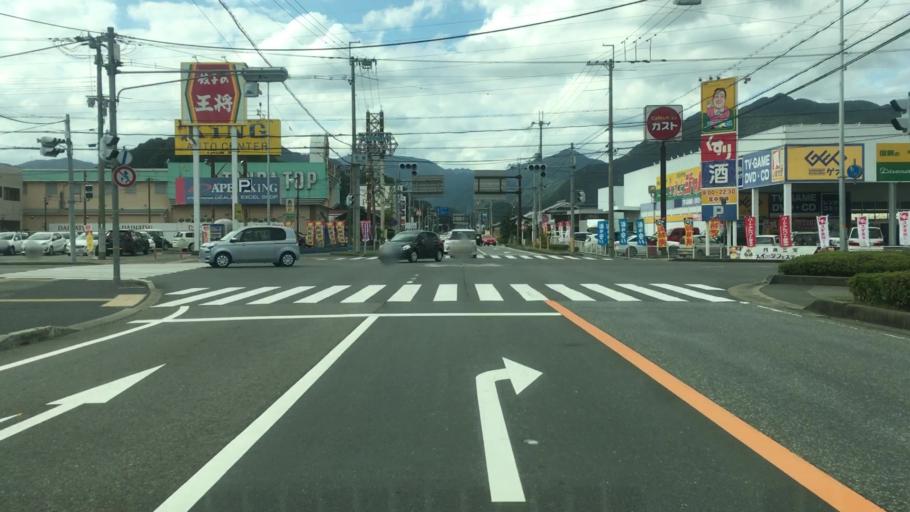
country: JP
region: Kyoto
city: Fukuchiyama
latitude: 35.1525
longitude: 135.0483
